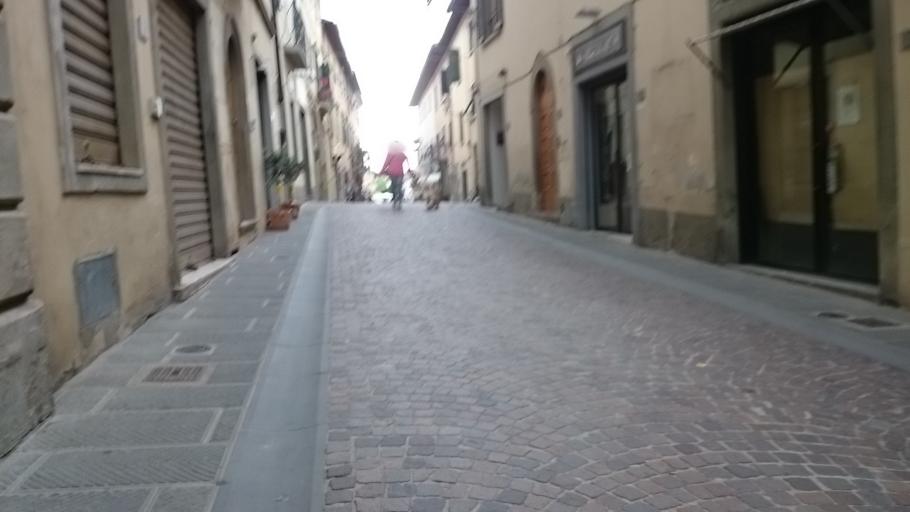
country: IT
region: Tuscany
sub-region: Province of Florence
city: Greve in Chianti
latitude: 43.5829
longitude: 11.3167
